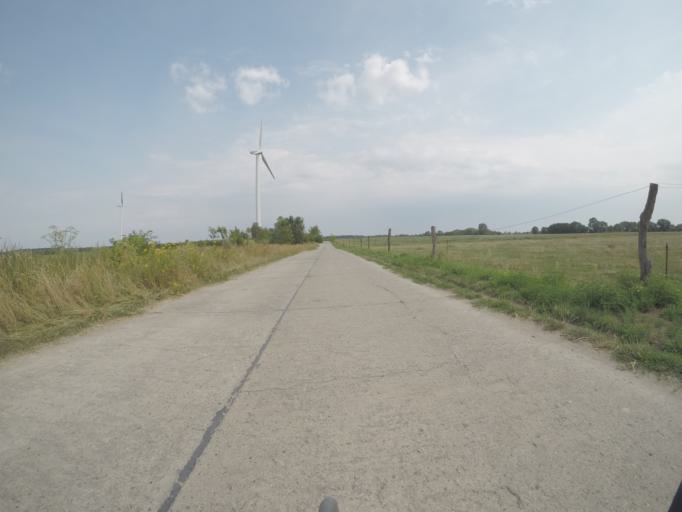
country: DE
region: Berlin
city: Blankenfelde
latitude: 52.6633
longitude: 13.4261
